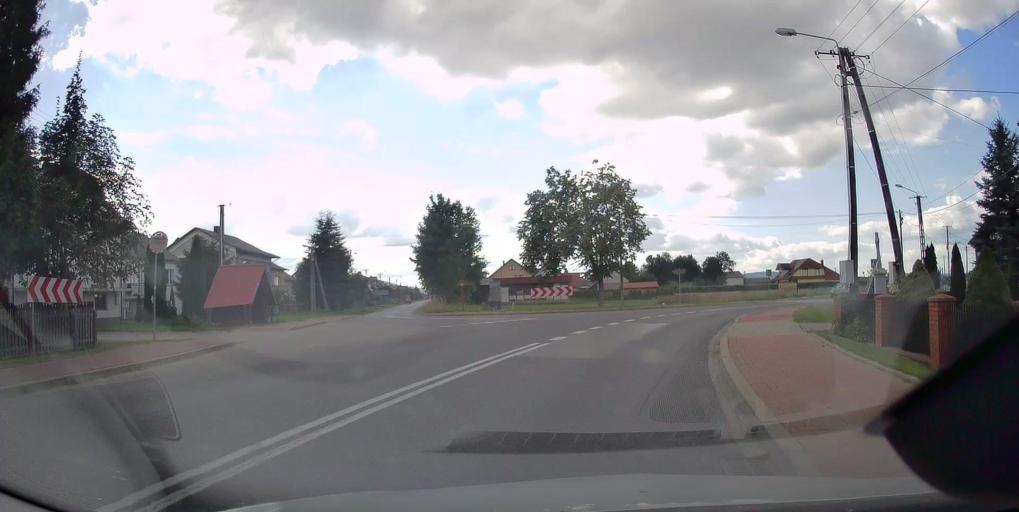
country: PL
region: Swietokrzyskie
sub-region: Powiat kielecki
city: Nowa Slupia
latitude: 50.8932
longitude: 21.0248
